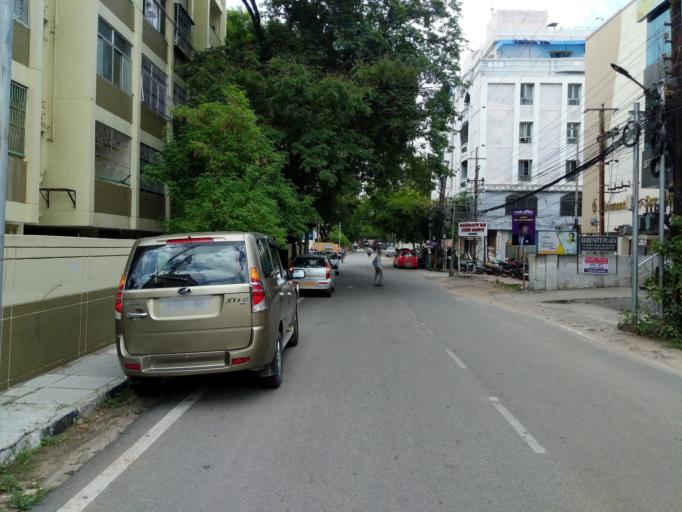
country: IN
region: Telangana
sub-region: Hyderabad
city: Hyderabad
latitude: 17.4371
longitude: 78.4527
